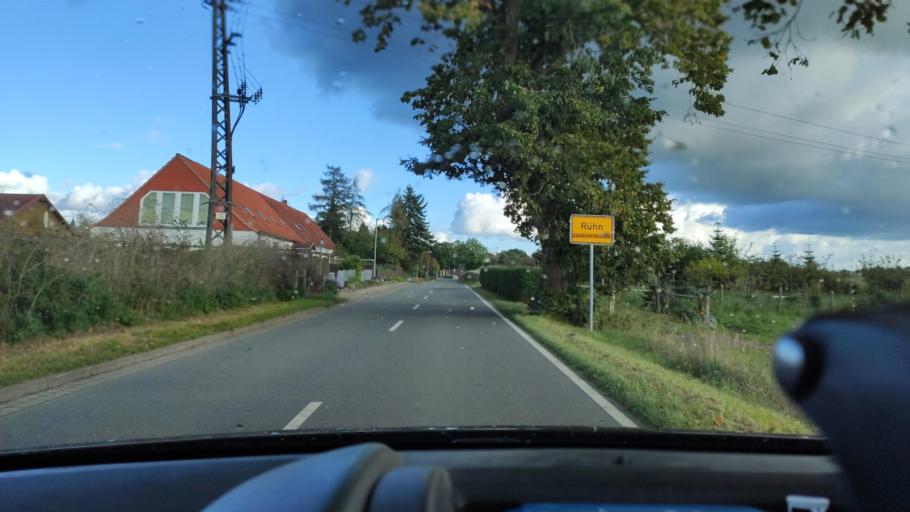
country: DE
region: Mecklenburg-Vorpommern
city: Butzow
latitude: 53.8231
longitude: 11.9318
